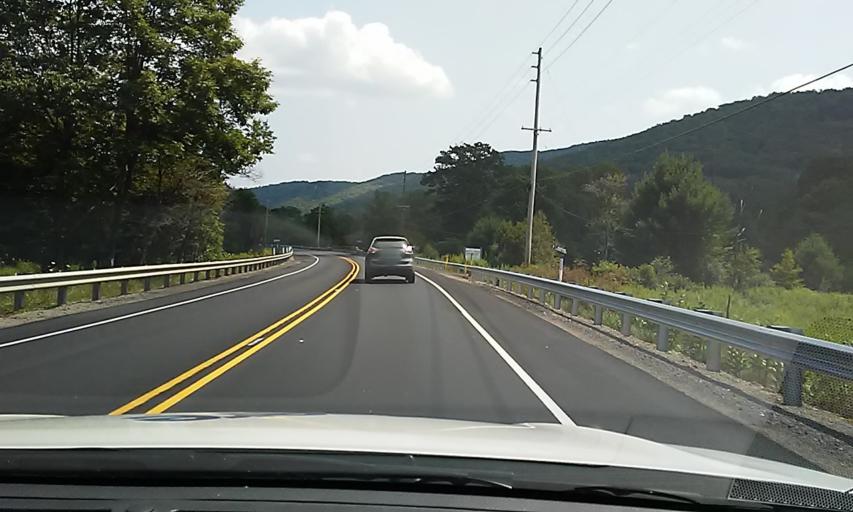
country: US
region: Pennsylvania
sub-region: Cameron County
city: Emporium
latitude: 41.4748
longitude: -78.3606
